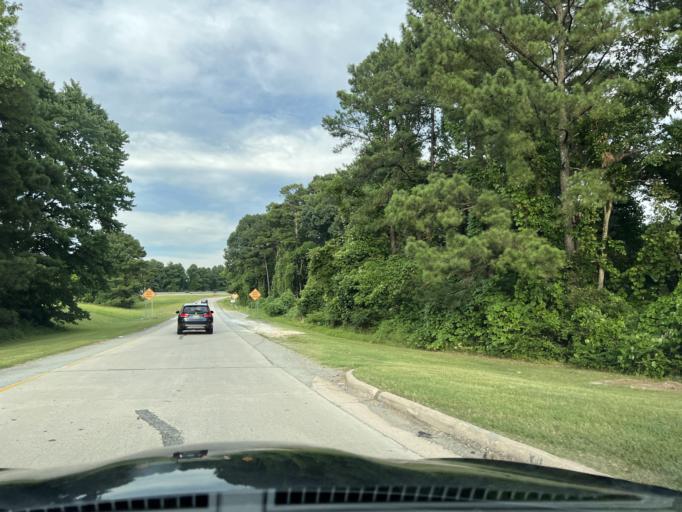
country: US
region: North Carolina
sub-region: Durham County
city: Durham
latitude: 35.9742
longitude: -78.8760
